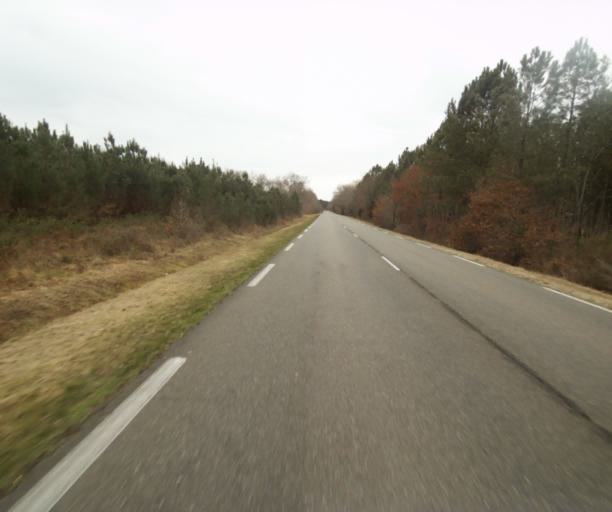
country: FR
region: Midi-Pyrenees
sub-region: Departement du Gers
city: Cazaubon
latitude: 44.0361
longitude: -0.1008
